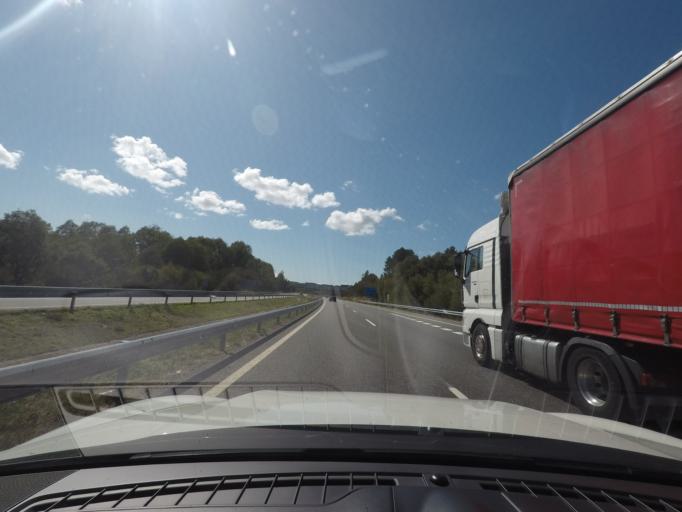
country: ES
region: Galicia
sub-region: Provincia de Ourense
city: Rios
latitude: 41.9814
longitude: -7.2941
